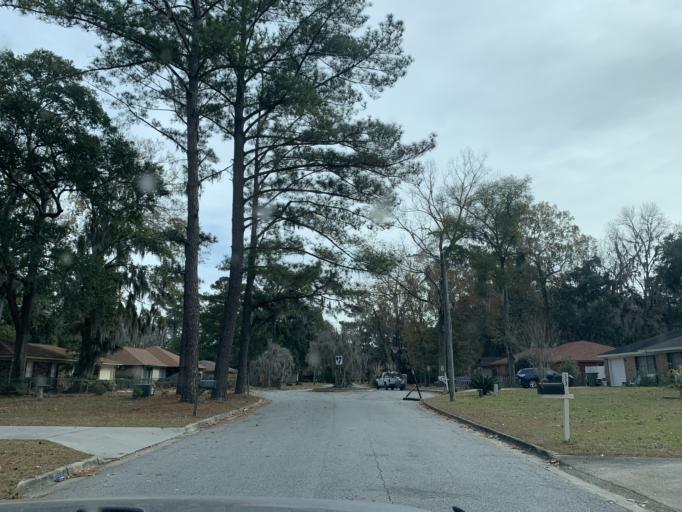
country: US
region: Georgia
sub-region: Chatham County
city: Montgomery
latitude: 31.9678
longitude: -81.1307
